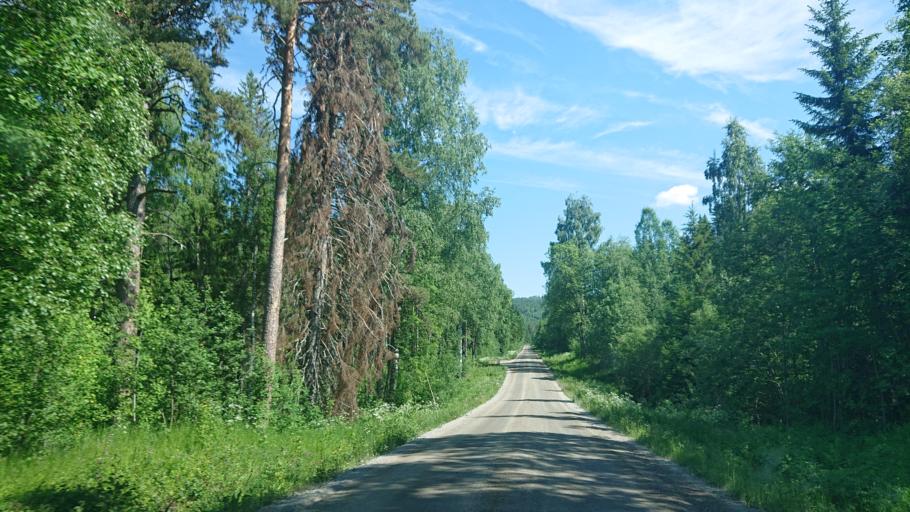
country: SE
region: Vaesternorrland
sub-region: Solleftea Kommun
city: Solleftea
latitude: 62.9706
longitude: 17.1659
